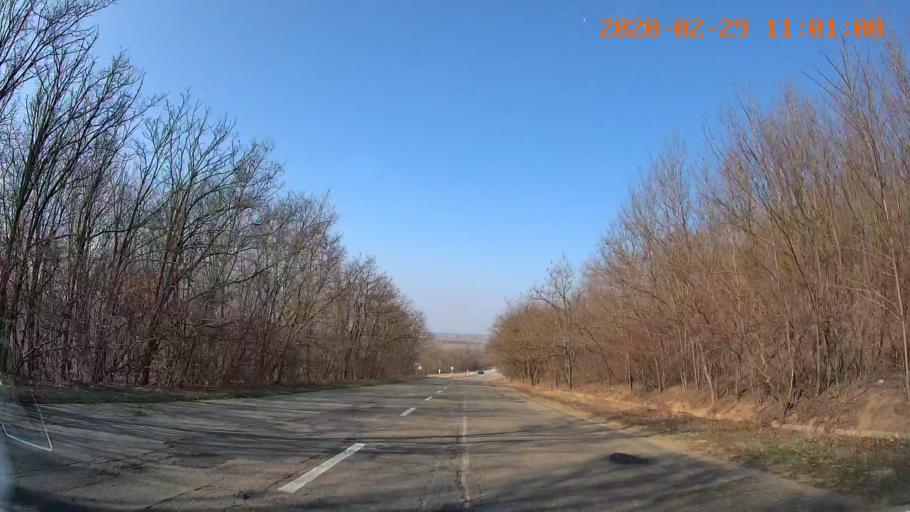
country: MD
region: Telenesti
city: Grigoriopol
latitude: 47.1613
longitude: 29.2665
